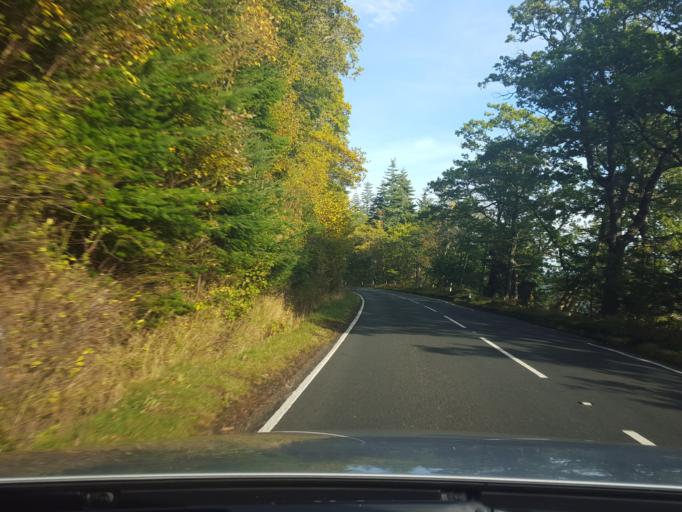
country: GB
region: Scotland
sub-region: Highland
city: Beauly
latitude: 57.2721
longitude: -4.5024
